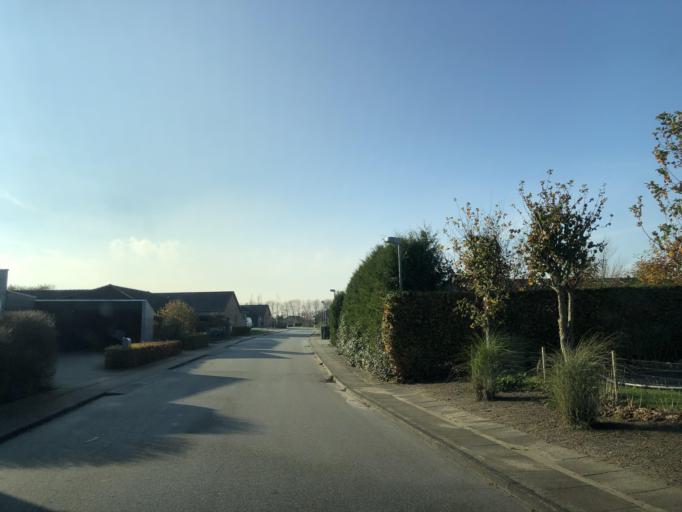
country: DK
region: Central Jutland
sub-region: Holstebro Kommune
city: Vinderup
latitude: 56.4021
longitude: 8.7573
